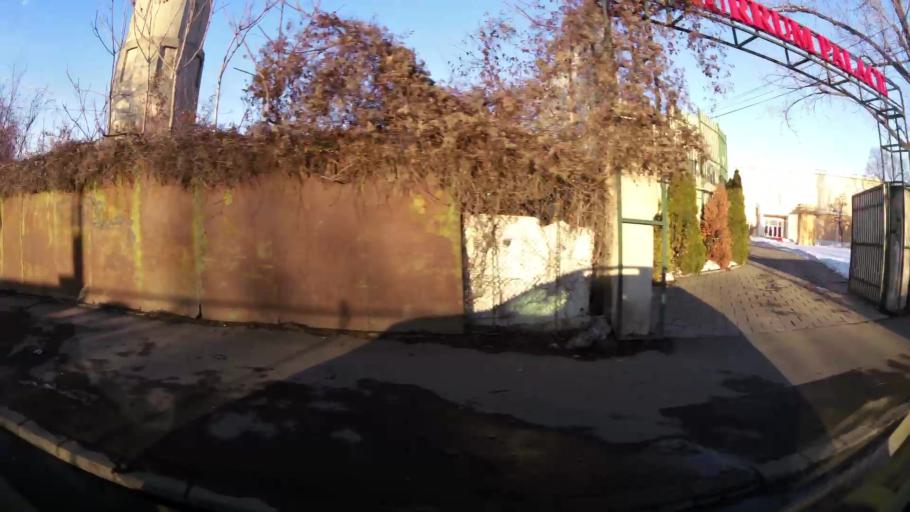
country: RO
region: Ilfov
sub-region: Comuna Fundeni-Dobroesti
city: Fundeni
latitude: 44.4520
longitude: 26.1359
